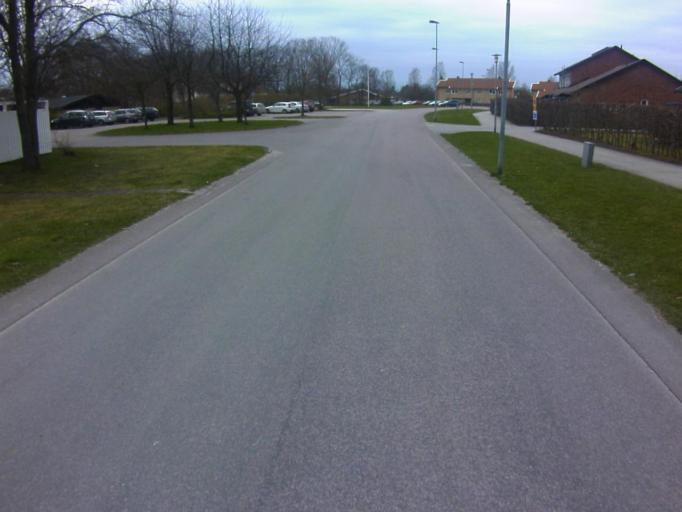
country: SE
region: Skane
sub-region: Kavlinge Kommun
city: Kaevlinge
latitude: 55.7955
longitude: 13.0961
